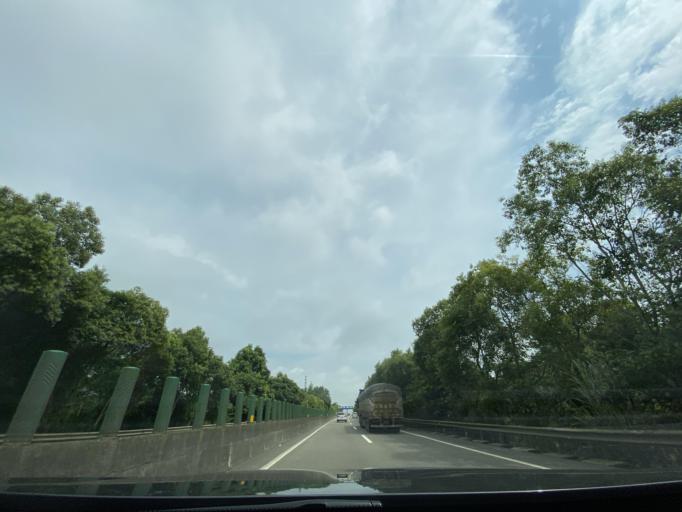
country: CN
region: Sichuan
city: Chonglong
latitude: 29.7331
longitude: 104.9150
